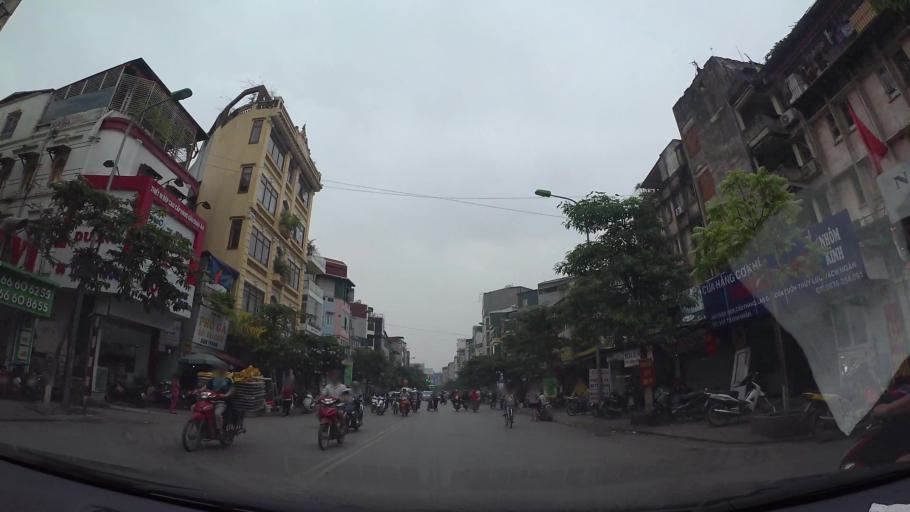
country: VN
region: Ha Noi
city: Hai BaTrung
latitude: 21.0028
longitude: 105.8533
